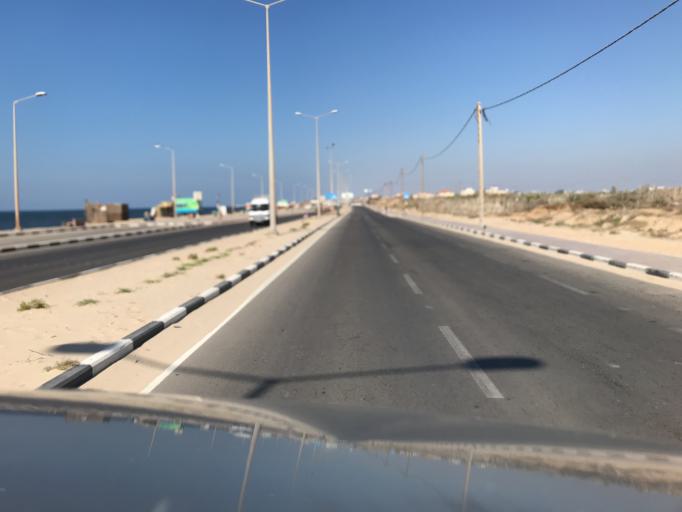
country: PS
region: Gaza Strip
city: An Nusayrat
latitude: 31.4727
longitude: 34.3852
